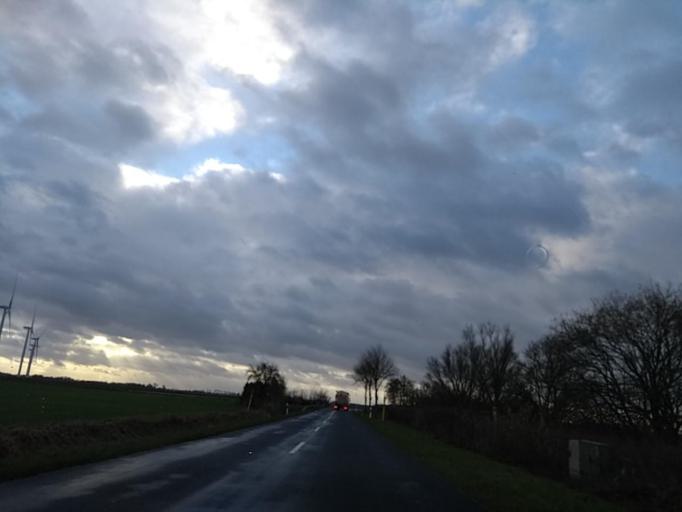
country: DE
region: Lower Saxony
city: Bunde
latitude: 53.2078
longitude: 7.2206
